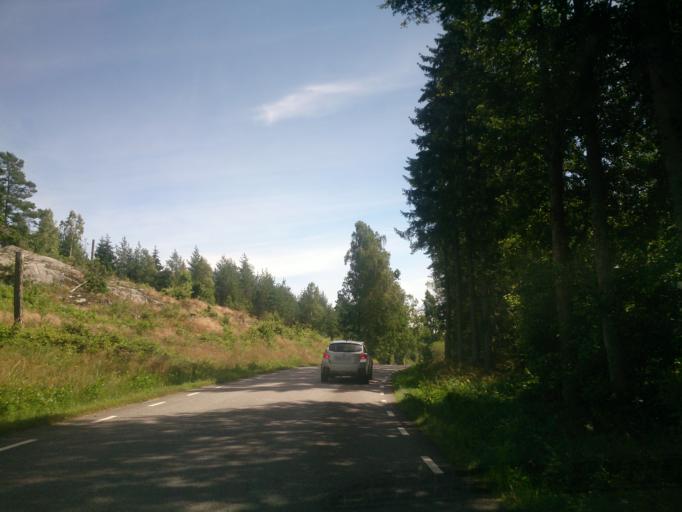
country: SE
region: OEstergoetland
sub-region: Valdemarsviks Kommun
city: Valdemarsvik
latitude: 58.2729
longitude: 16.7251
